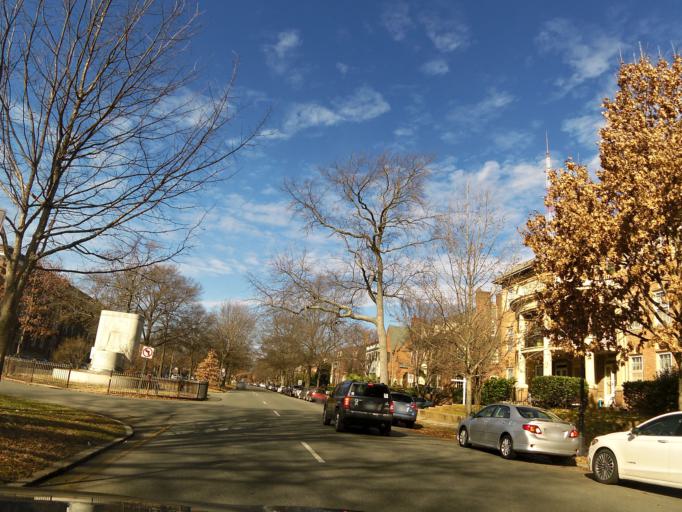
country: US
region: Virginia
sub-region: City of Richmond
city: Richmond
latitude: 37.5626
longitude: -77.4746
